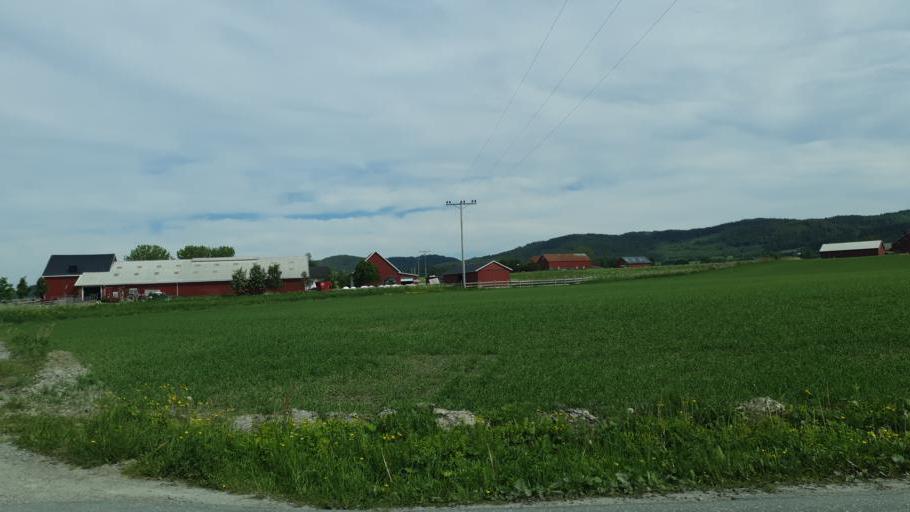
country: NO
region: Sor-Trondelag
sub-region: Rissa
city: Rissa
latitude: 63.5742
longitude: 9.9340
